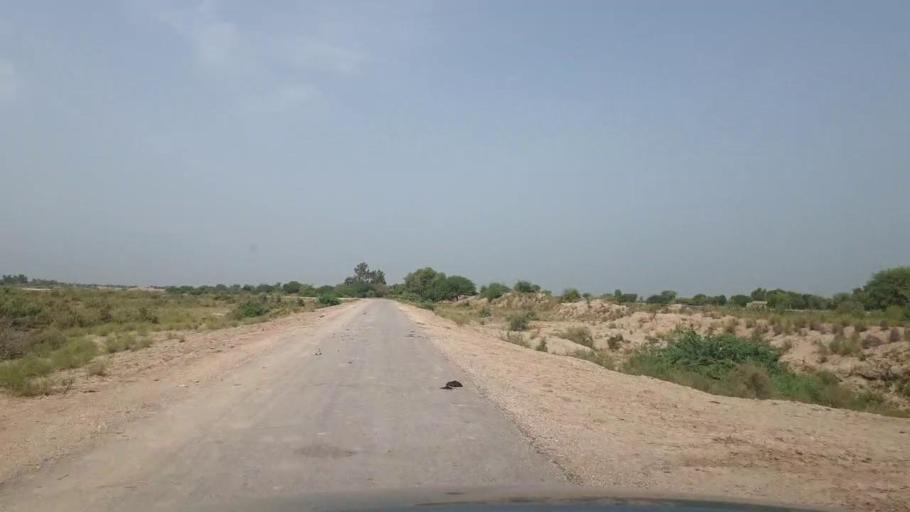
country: PK
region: Sindh
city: Madeji
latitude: 27.8398
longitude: 68.4339
